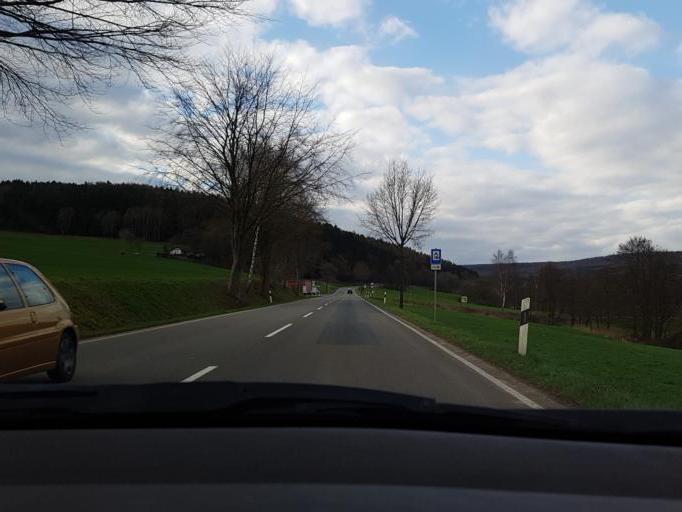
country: DE
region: Lower Saxony
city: Bodenfelde
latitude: 51.6961
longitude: 9.5528
